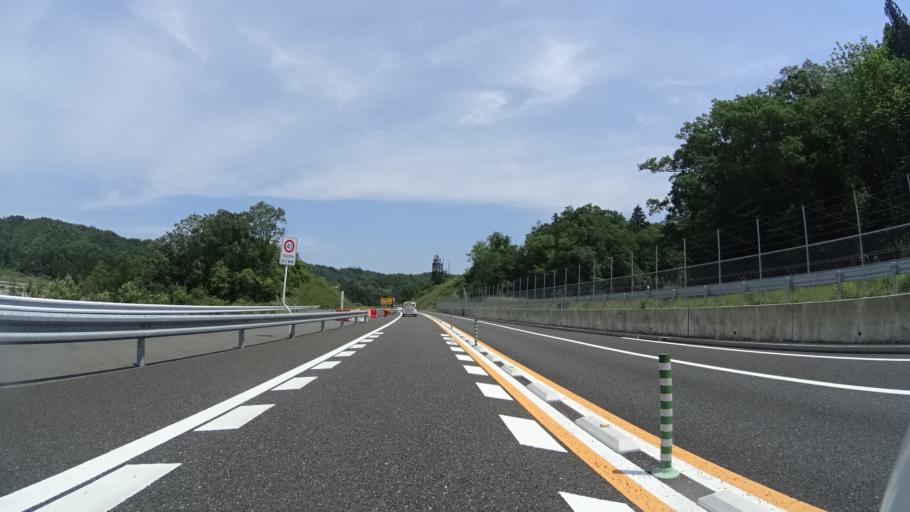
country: JP
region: Kyoto
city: Miyazu
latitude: 35.5725
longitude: 135.1213
